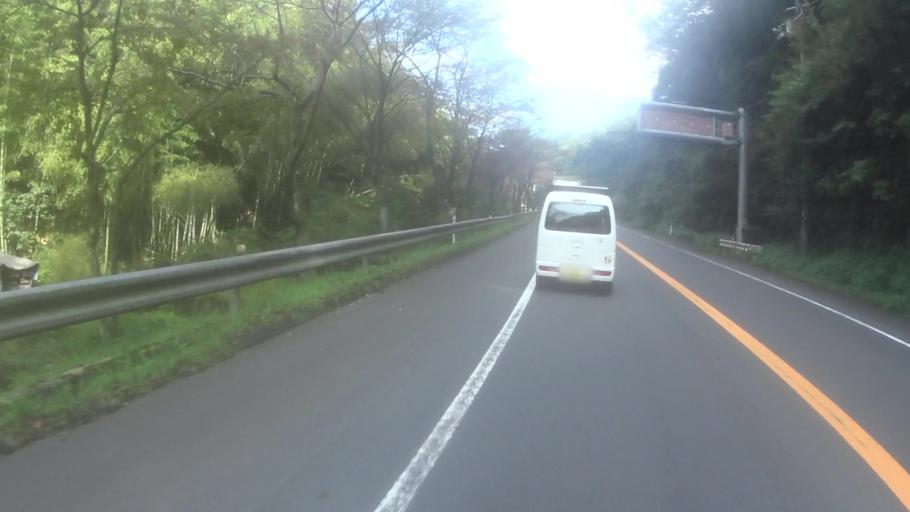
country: JP
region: Kyoto
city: Miyazu
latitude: 35.5438
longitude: 135.1112
